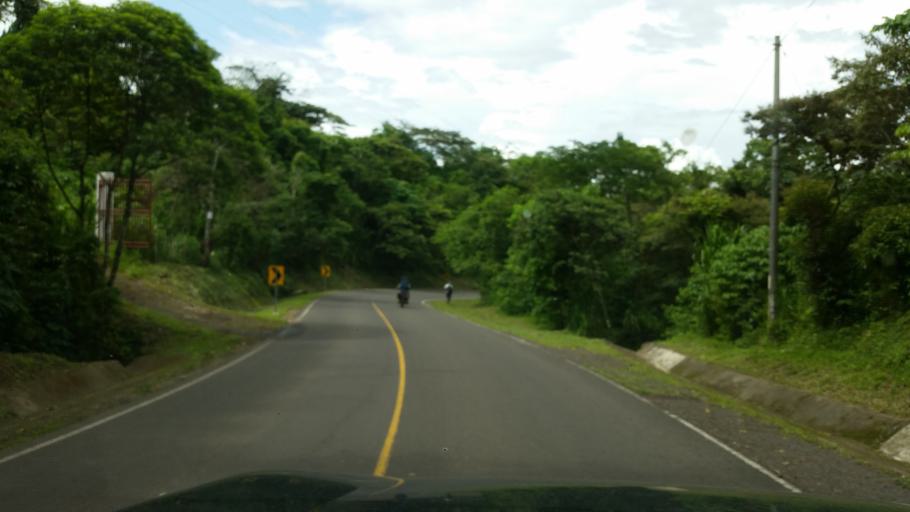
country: NI
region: Matagalpa
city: San Ramon
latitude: 12.9687
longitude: -85.8523
